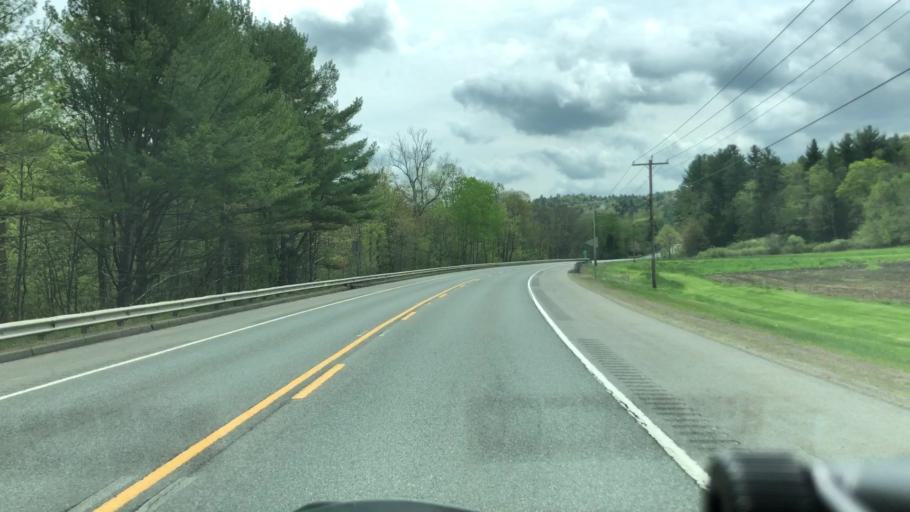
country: US
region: Massachusetts
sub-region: Hampshire County
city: Chesterfield
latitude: 42.4698
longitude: -72.9078
